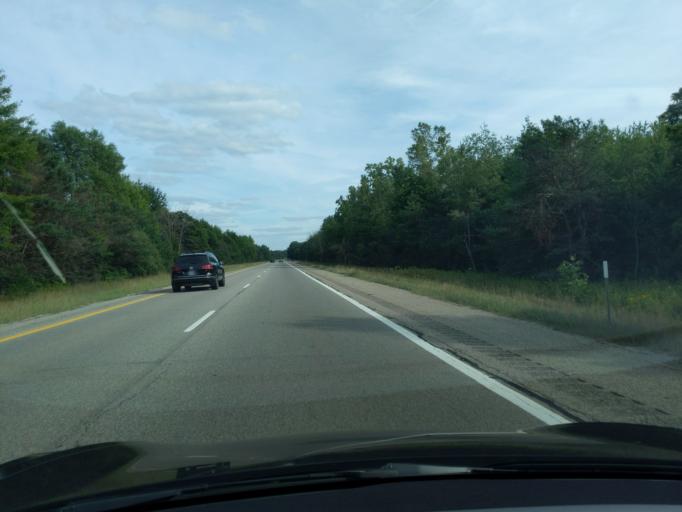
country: US
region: Michigan
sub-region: Muskegon County
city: Fruitport
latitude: 43.0987
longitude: -86.1073
